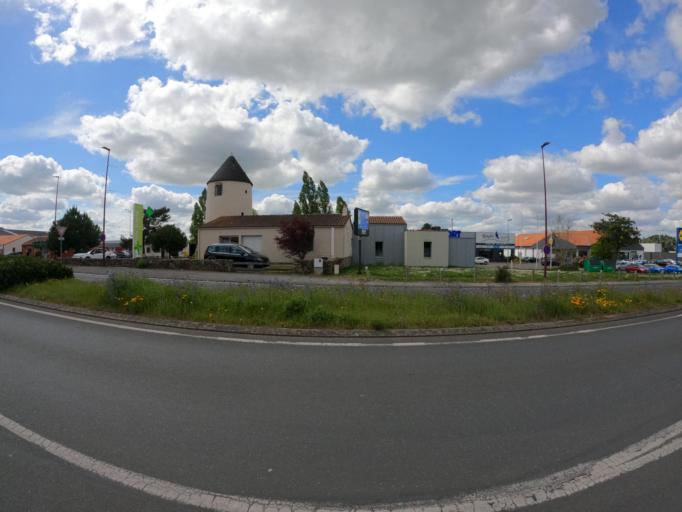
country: FR
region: Pays de la Loire
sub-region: Departement de la Loire-Atlantique
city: Clisson
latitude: 47.0962
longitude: -1.2817
